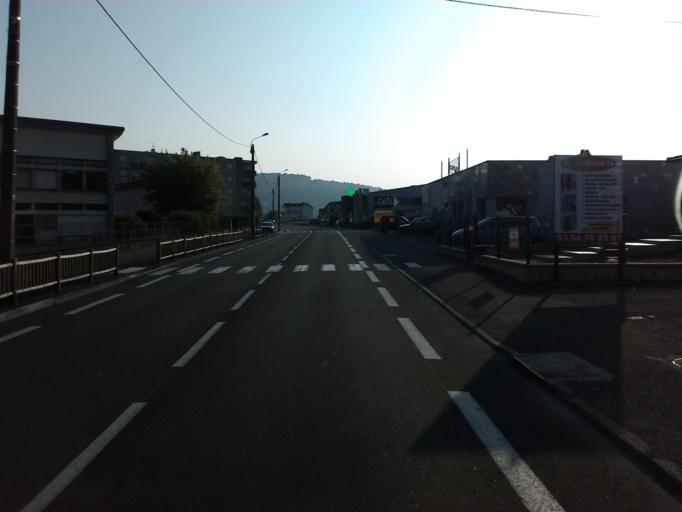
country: FR
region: Franche-Comte
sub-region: Departement de la Haute-Saone
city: Vesoul
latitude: 47.6204
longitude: 6.1678
